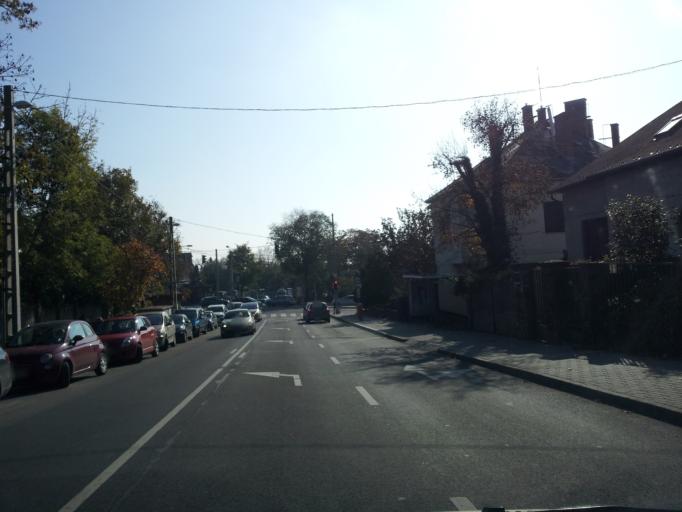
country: HU
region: Budapest
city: Budapest XII. keruelet
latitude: 47.4822
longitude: 18.9979
